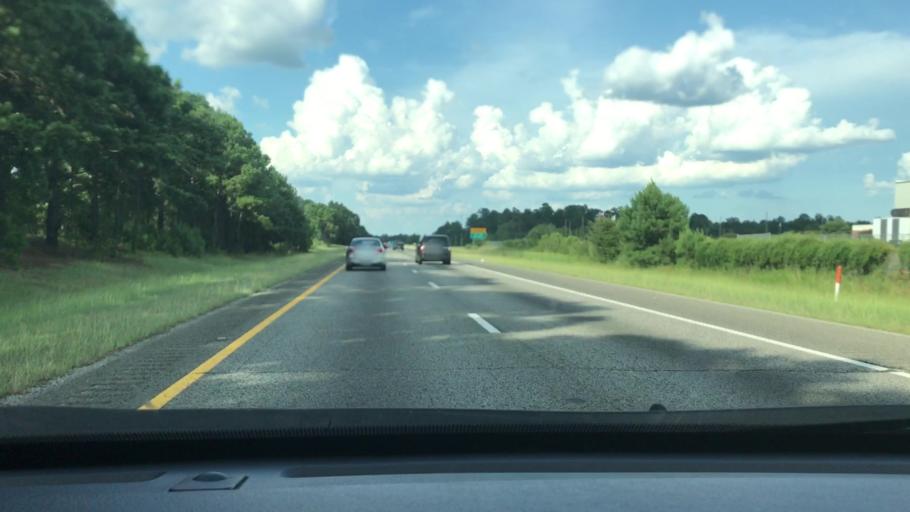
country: US
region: South Carolina
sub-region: Florence County
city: Florence
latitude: 34.2762
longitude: -79.6907
